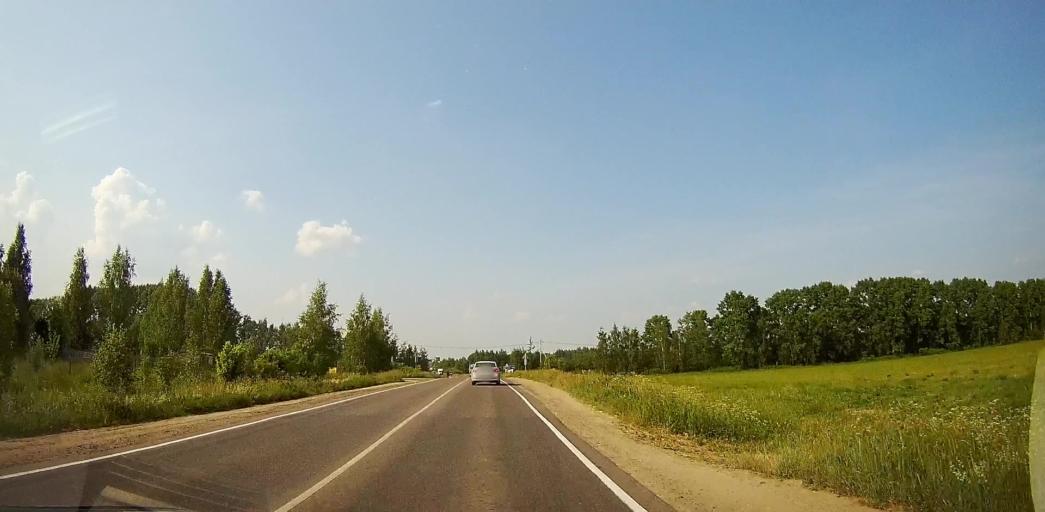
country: RU
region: Moskovskaya
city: Zhitnevo
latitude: 55.3196
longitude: 37.9001
